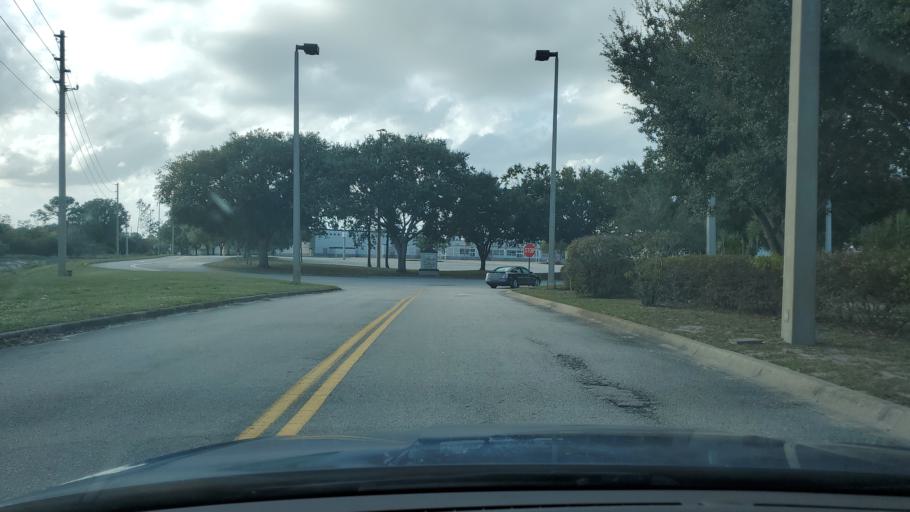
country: US
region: Florida
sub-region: Highlands County
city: Sebring
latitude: 27.4879
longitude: -81.4841
